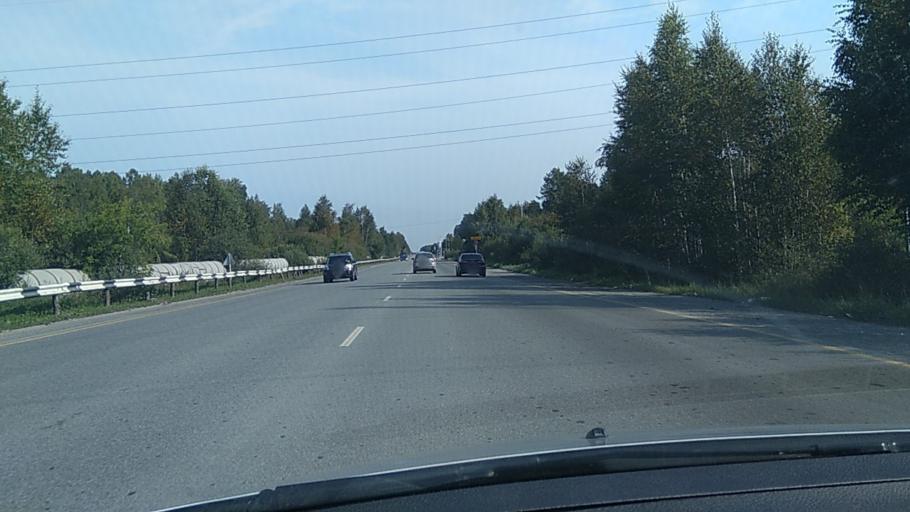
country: RU
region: Sverdlovsk
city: Sredneuralsk
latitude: 56.9884
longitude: 60.5001
